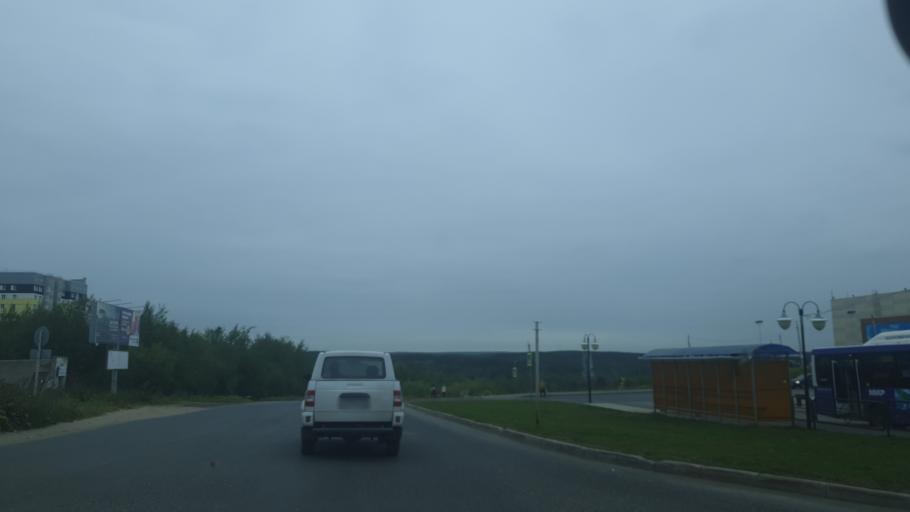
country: RU
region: Komi Republic
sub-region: Syktyvdinskiy Rayon
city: Syktyvkar
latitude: 61.6966
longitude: 50.8052
